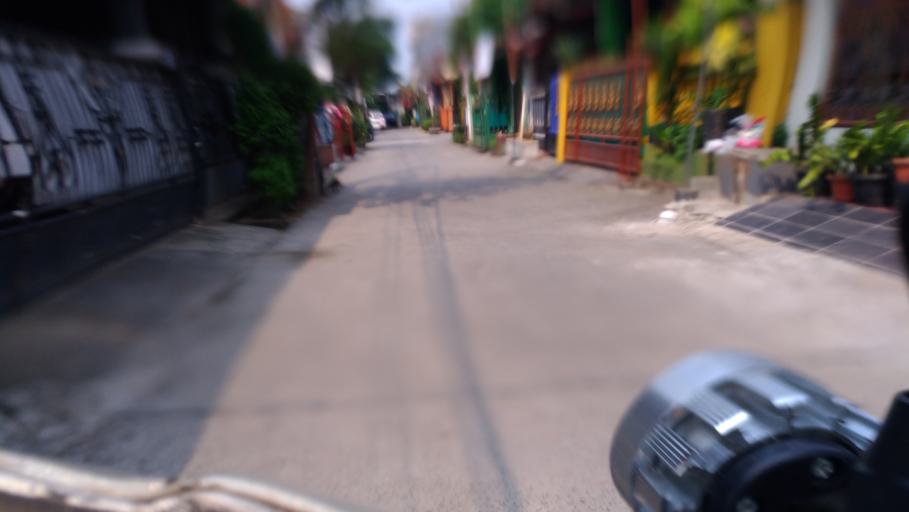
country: ID
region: West Java
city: Depok
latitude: -6.3606
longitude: 106.8702
